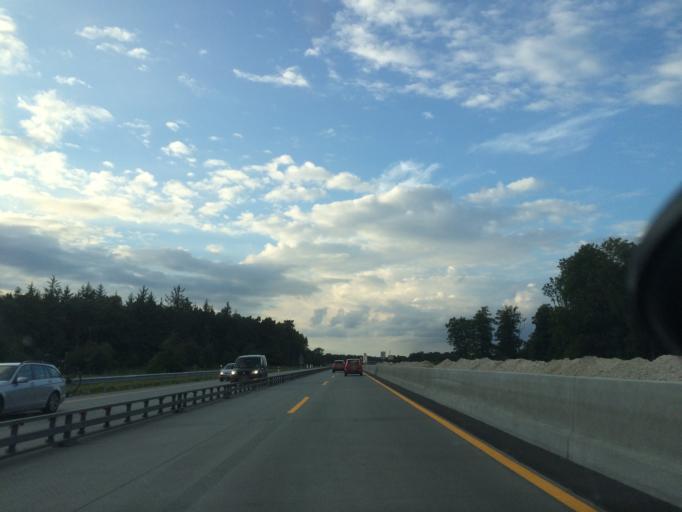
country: DE
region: Schleswig-Holstein
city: Grossenaspe
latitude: 53.9904
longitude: 9.9393
